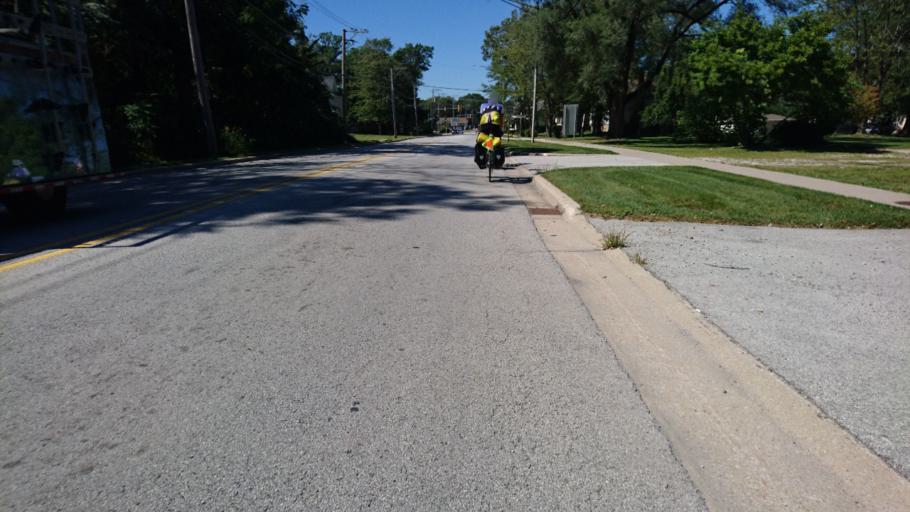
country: US
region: Illinois
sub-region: Cook County
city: Glenwood
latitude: 41.5431
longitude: -87.6094
